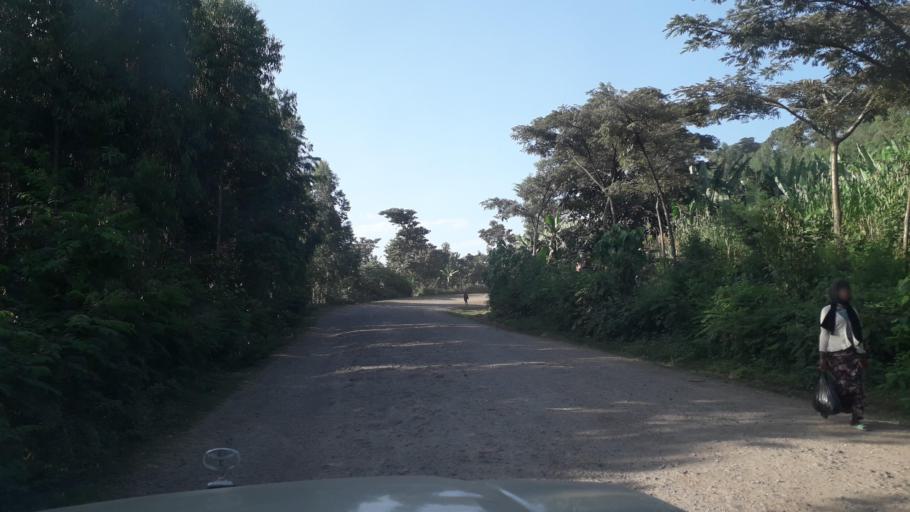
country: ET
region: Oromiya
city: Jima
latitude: 7.4849
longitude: 36.8760
